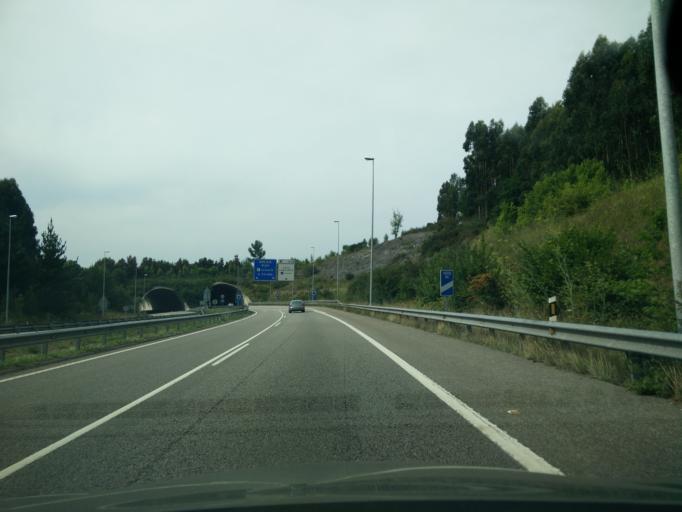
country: ES
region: Asturias
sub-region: Province of Asturias
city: Arriba
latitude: 43.5081
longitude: -5.5954
